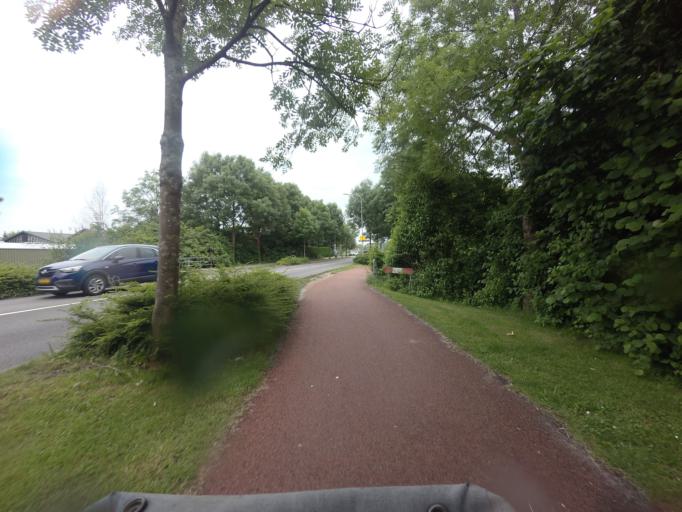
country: NL
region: North Holland
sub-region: Gemeente Enkhuizen
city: Enkhuizen
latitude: 52.6984
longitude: 5.2322
